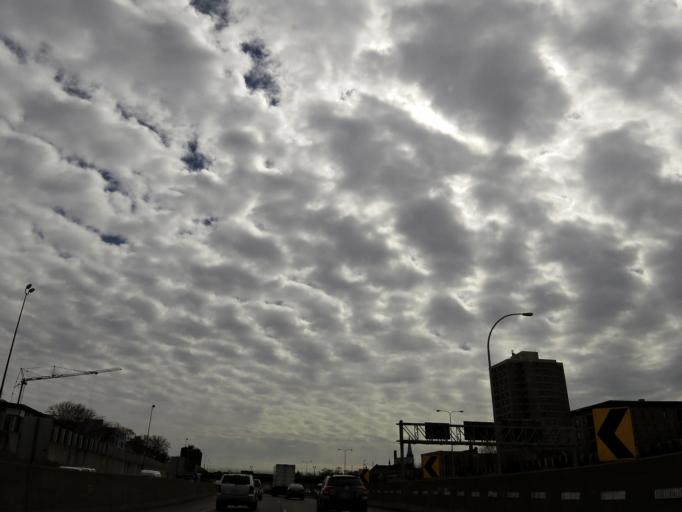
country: US
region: Minnesota
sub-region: Hennepin County
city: Minneapolis
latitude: 44.9648
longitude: -93.2694
